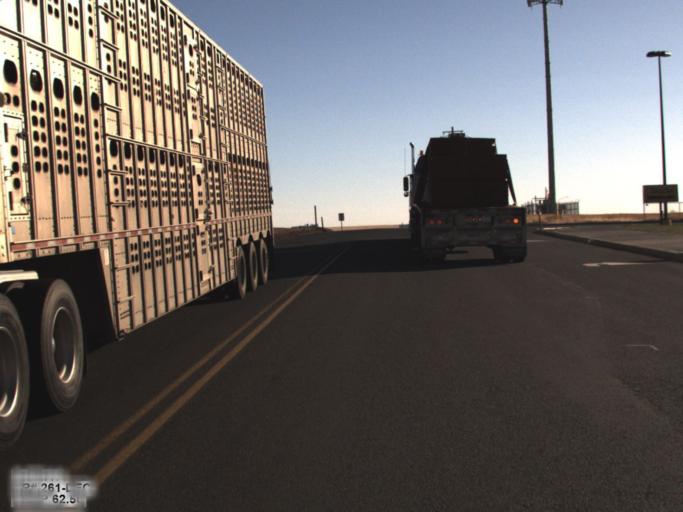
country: US
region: Washington
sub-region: Adams County
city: Ritzville
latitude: 47.1130
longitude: -118.3656
